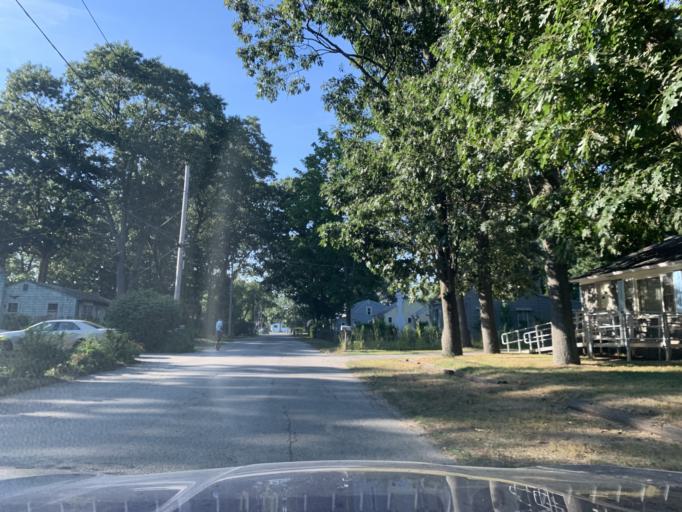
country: US
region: Rhode Island
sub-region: Kent County
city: Warwick
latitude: 41.6935
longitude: -71.4406
